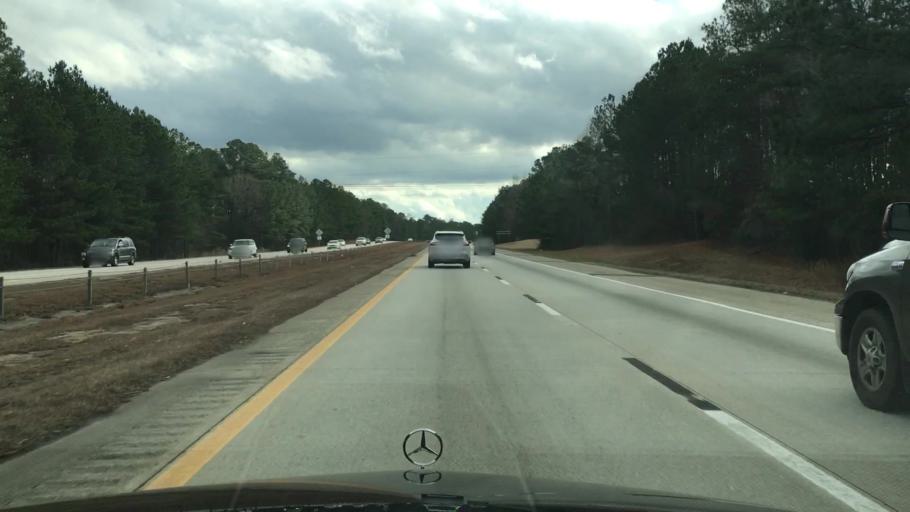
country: US
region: North Carolina
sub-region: Wake County
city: Garner
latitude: 35.6825
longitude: -78.5679
